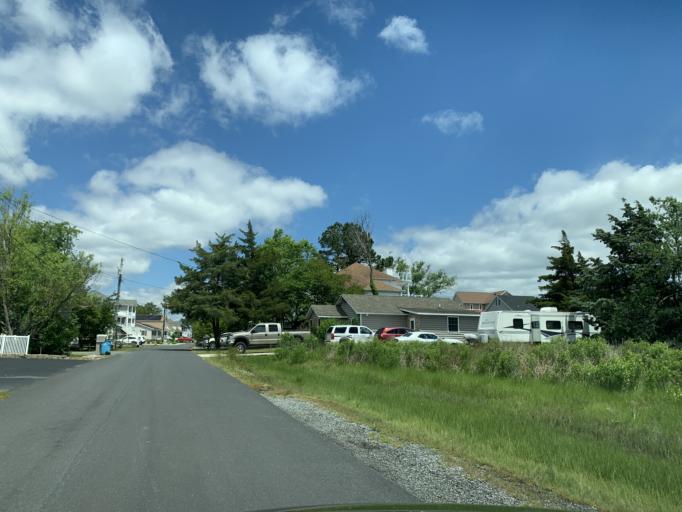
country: US
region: Maryland
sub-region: Worcester County
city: West Ocean City
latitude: 38.3566
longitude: -75.1178
